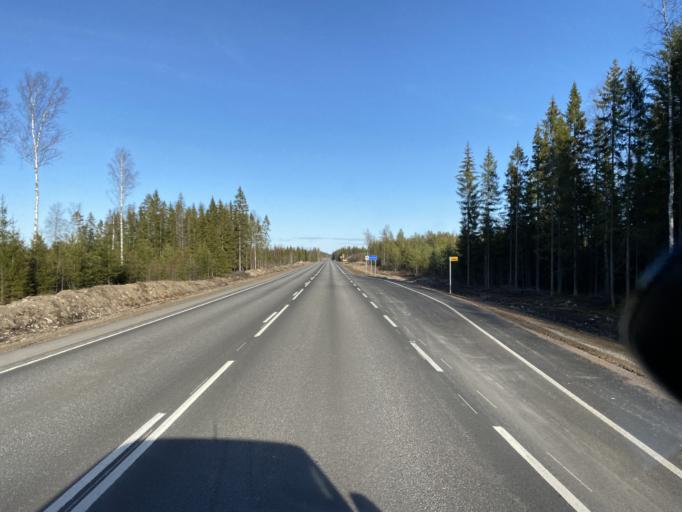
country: FI
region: Satakunta
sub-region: Pori
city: Kokemaeki
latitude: 61.1709
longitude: 22.4811
